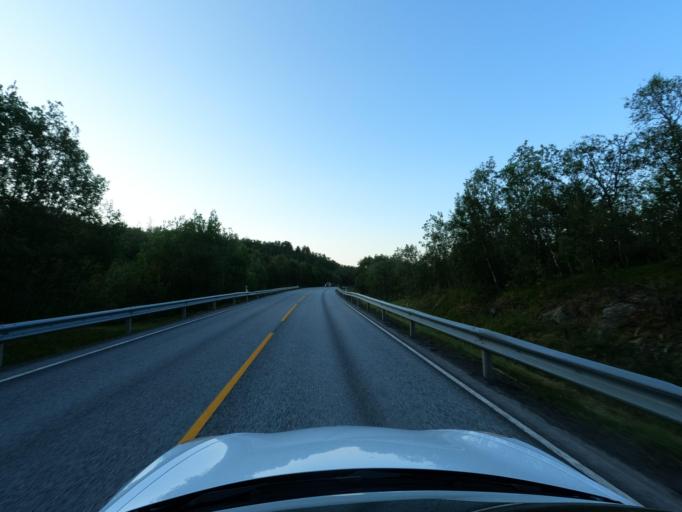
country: NO
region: Troms
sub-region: Harstad
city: Harstad
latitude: 68.7361
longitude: 16.5536
